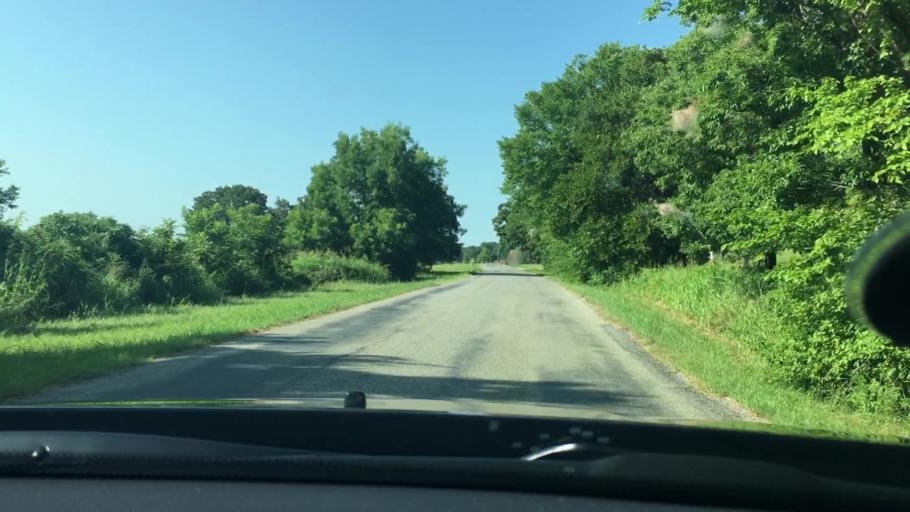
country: US
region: Oklahoma
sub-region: Pontotoc County
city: Byng
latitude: 34.8137
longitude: -96.6261
